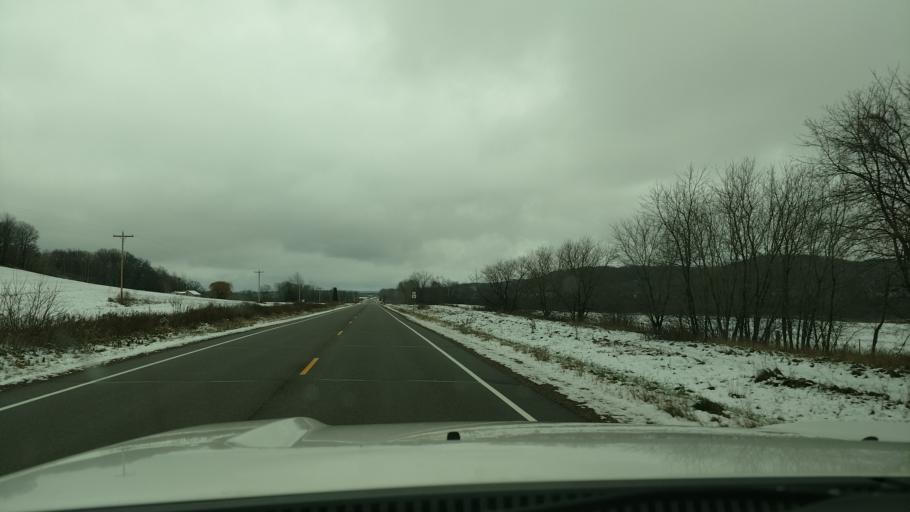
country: US
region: Wisconsin
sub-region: Dunn County
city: Colfax
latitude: 45.1371
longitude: -91.7945
